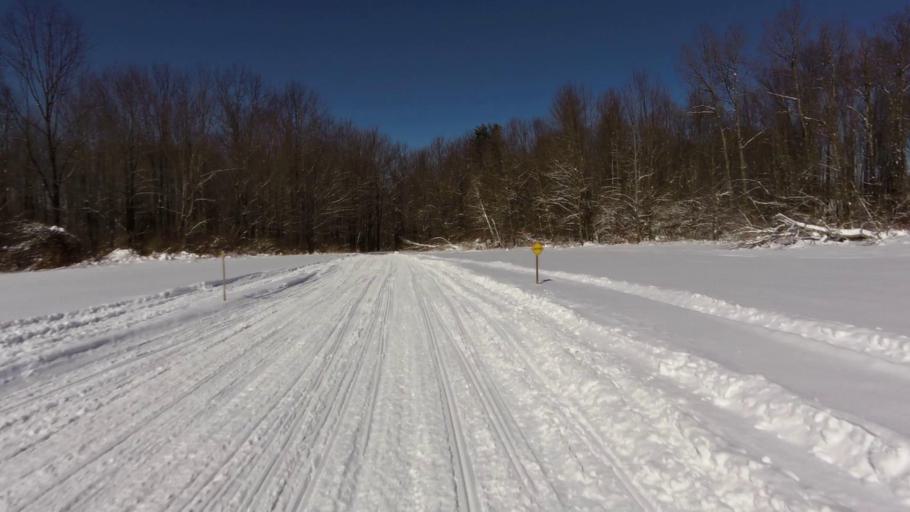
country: US
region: New York
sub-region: Chautauqua County
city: Mayville
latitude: 42.2337
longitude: -79.4199
